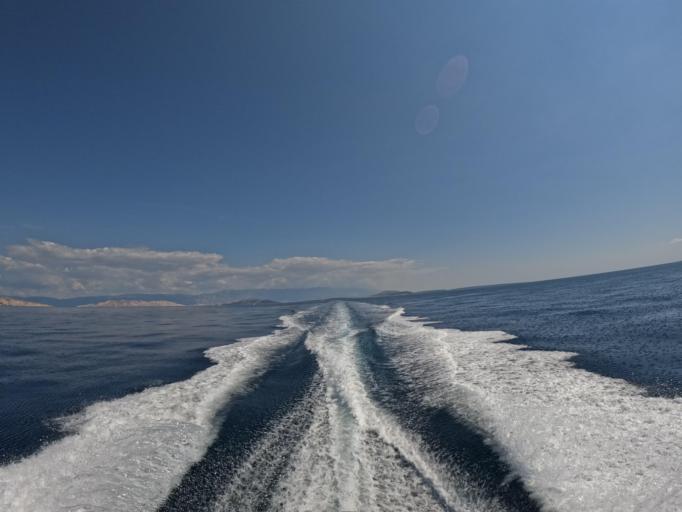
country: HR
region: Primorsko-Goranska
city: Punat
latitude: 44.9074
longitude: 14.5986
